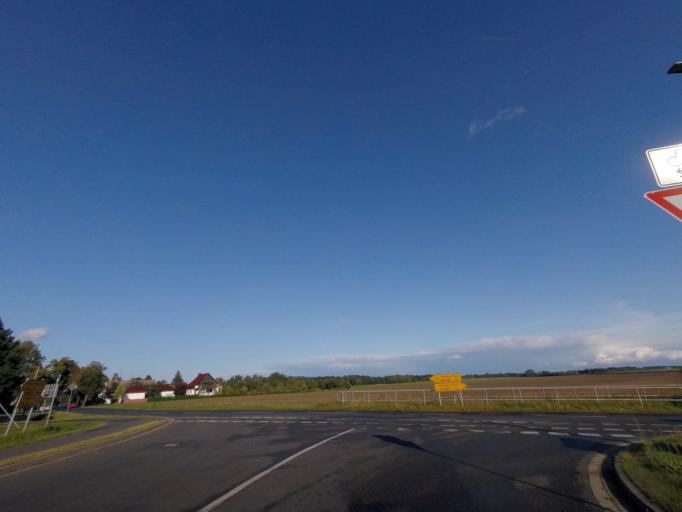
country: DE
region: Brandenburg
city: Niedergorsdorf
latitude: 51.9762
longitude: 12.9800
